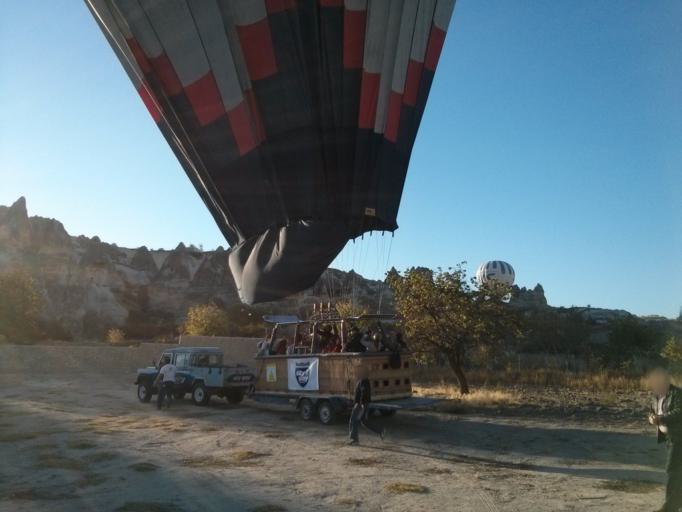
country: TR
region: Nevsehir
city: Goereme
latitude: 38.6427
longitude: 34.8377
